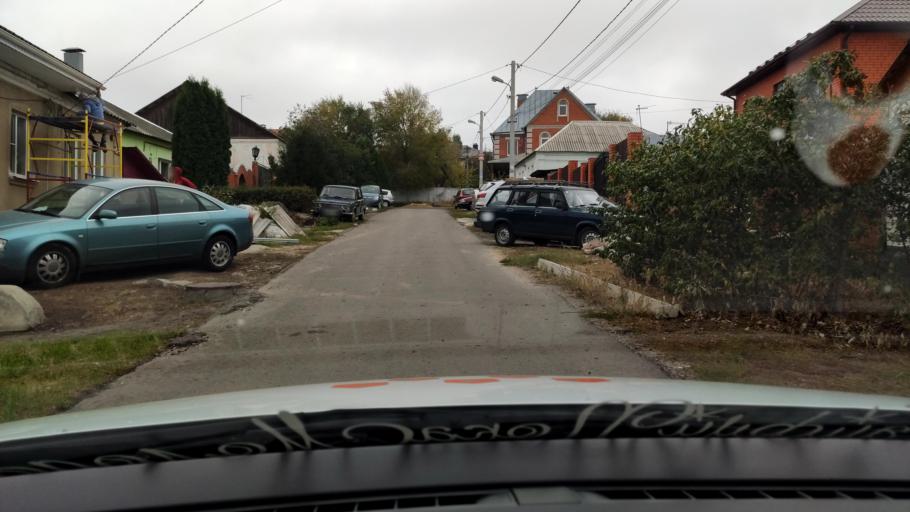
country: RU
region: Voronezj
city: Voronezh
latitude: 51.6348
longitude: 39.2000
